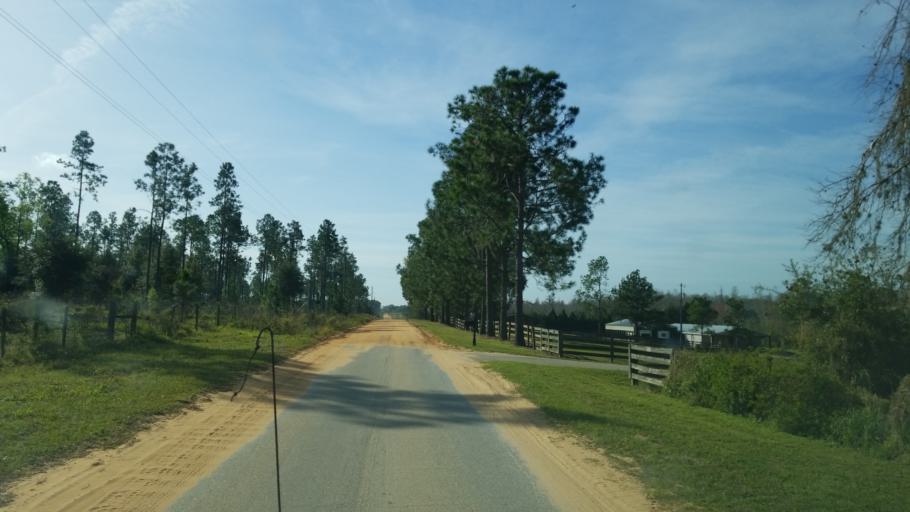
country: US
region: Florida
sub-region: Lake County
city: Clermont
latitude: 28.4597
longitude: -81.7569
